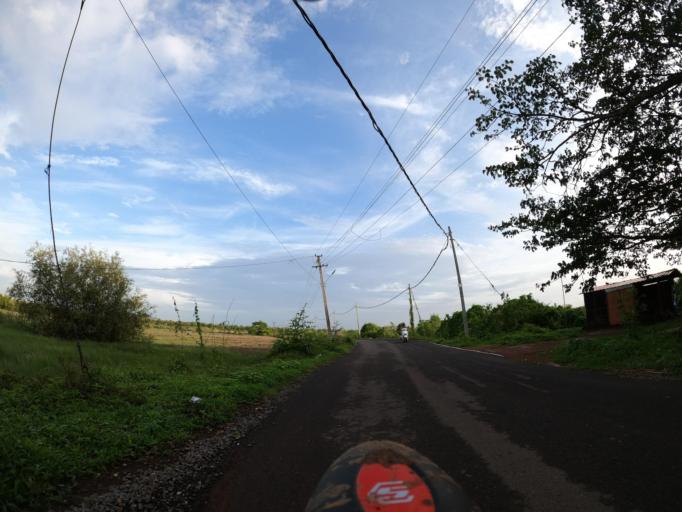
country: IN
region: Goa
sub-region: North Goa
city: Serula
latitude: 15.5312
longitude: 73.8578
